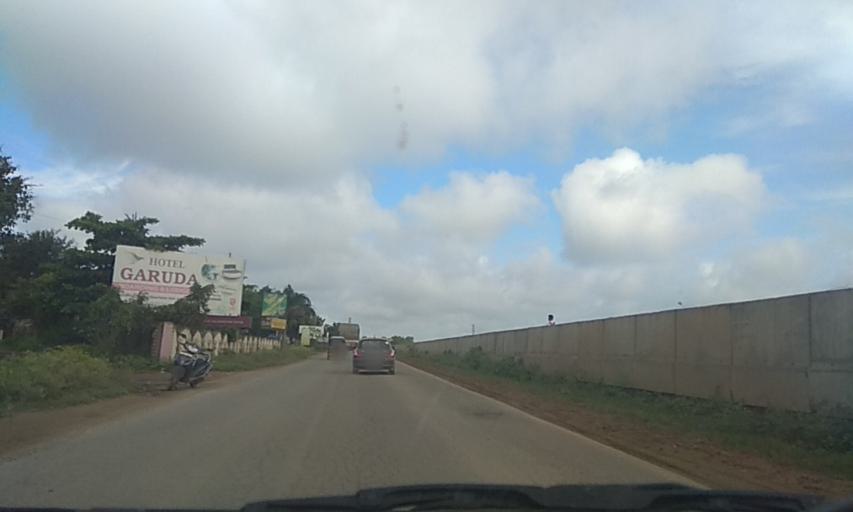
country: IN
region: Karnataka
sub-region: Haveri
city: Shiggaon
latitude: 14.9949
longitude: 75.2127
